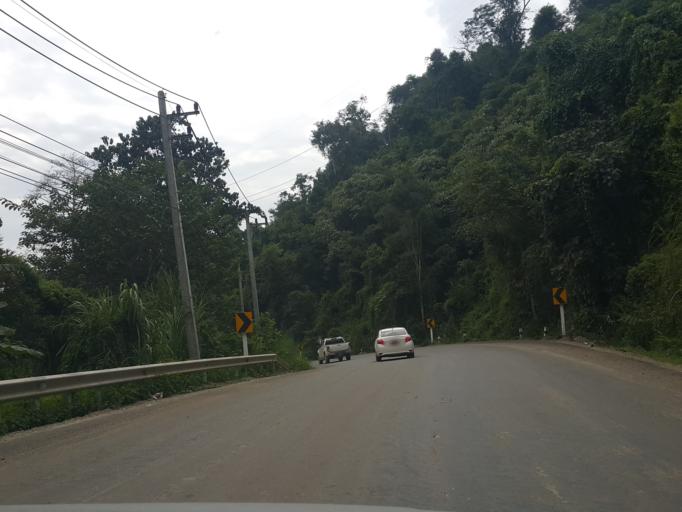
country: TH
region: Chiang Mai
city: Mae Taeng
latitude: 19.1753
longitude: 98.6924
